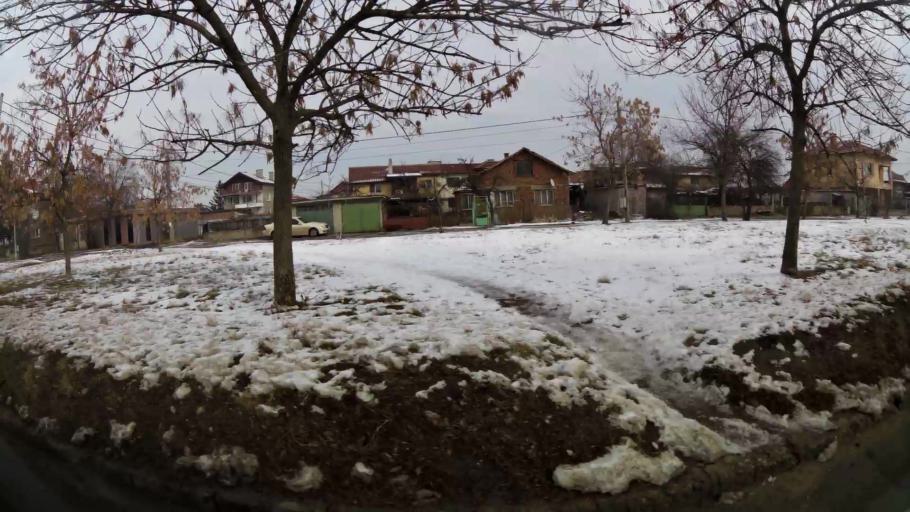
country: BG
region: Sofia-Capital
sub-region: Stolichna Obshtina
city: Sofia
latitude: 42.7126
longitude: 23.4056
